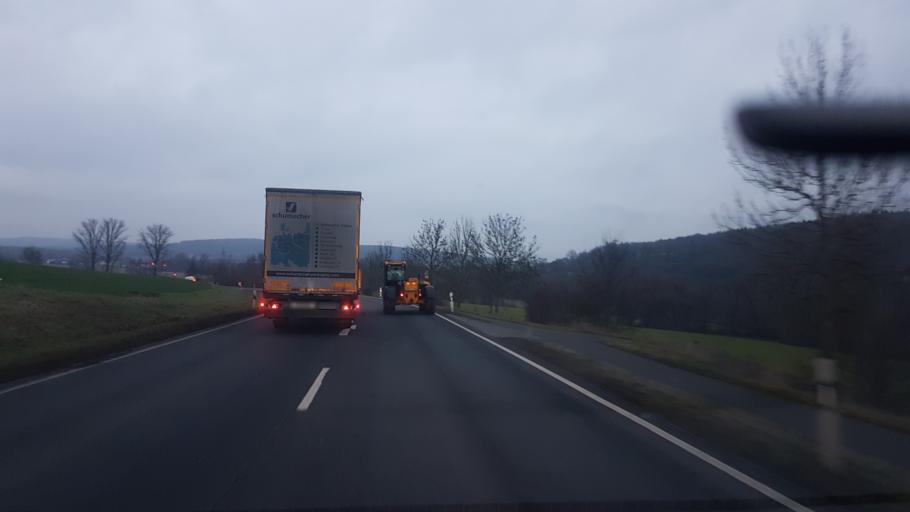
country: DE
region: Bavaria
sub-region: Regierungsbezirk Unterfranken
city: Rentweinsdorf
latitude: 50.0805
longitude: 10.7937
